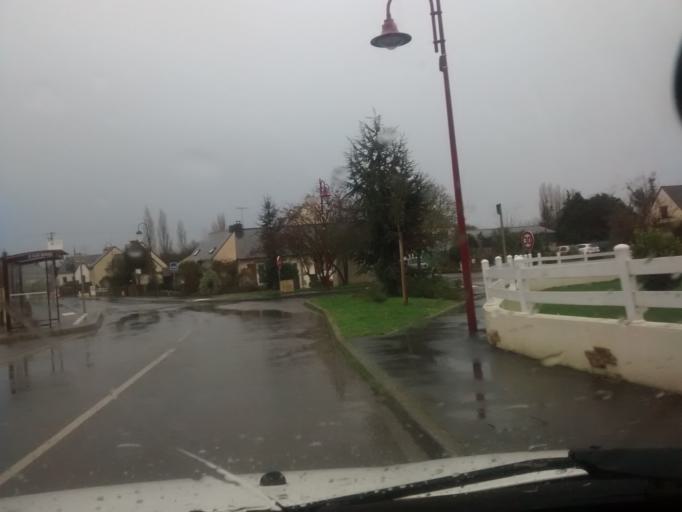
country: FR
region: Brittany
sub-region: Departement d'Ille-et-Vilaine
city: La Gouesniere
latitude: 48.5773
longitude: -1.8880
